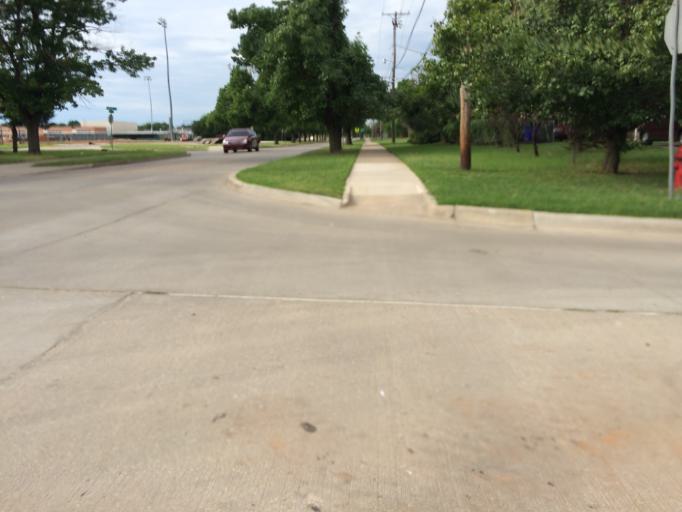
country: US
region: Oklahoma
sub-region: Cleveland County
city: Norman
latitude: 35.2226
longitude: -97.4591
